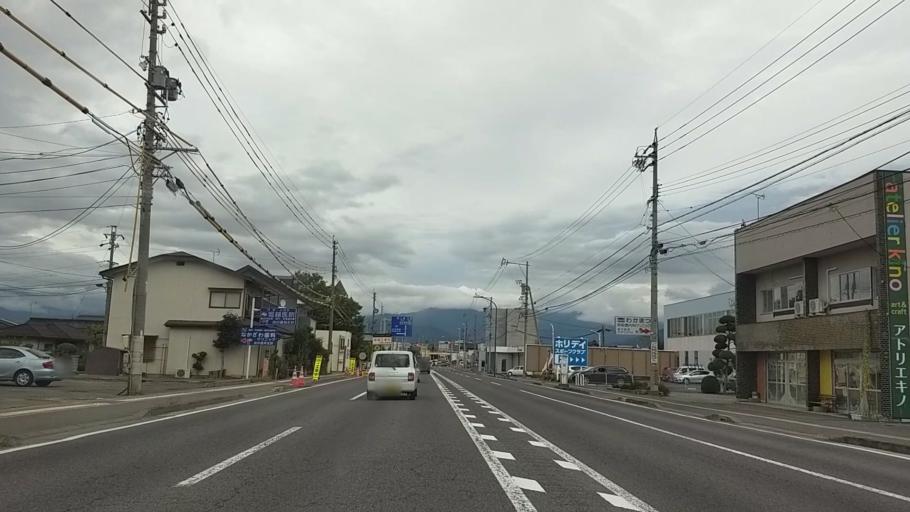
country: JP
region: Nagano
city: Nagano-shi
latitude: 36.6478
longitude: 138.2135
